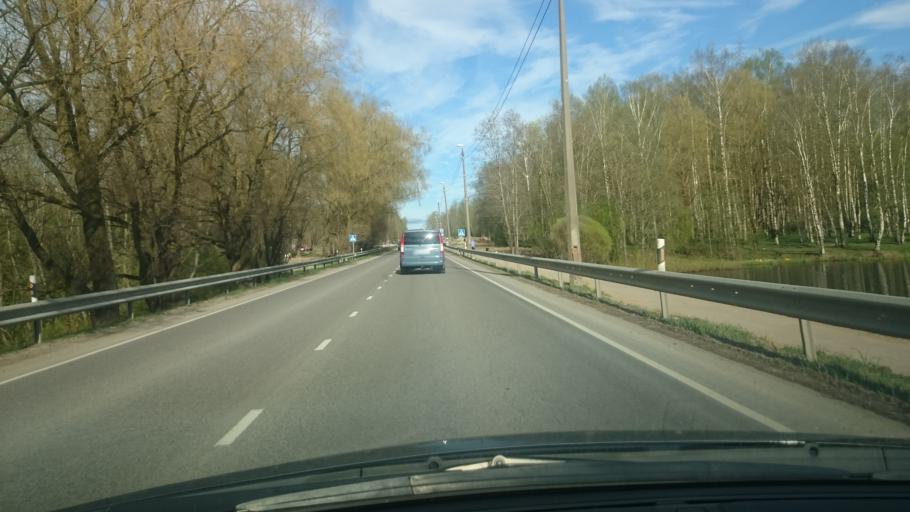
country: EE
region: Ida-Virumaa
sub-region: Sillamaee linn
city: Sillamae
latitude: 59.3910
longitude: 27.7592
